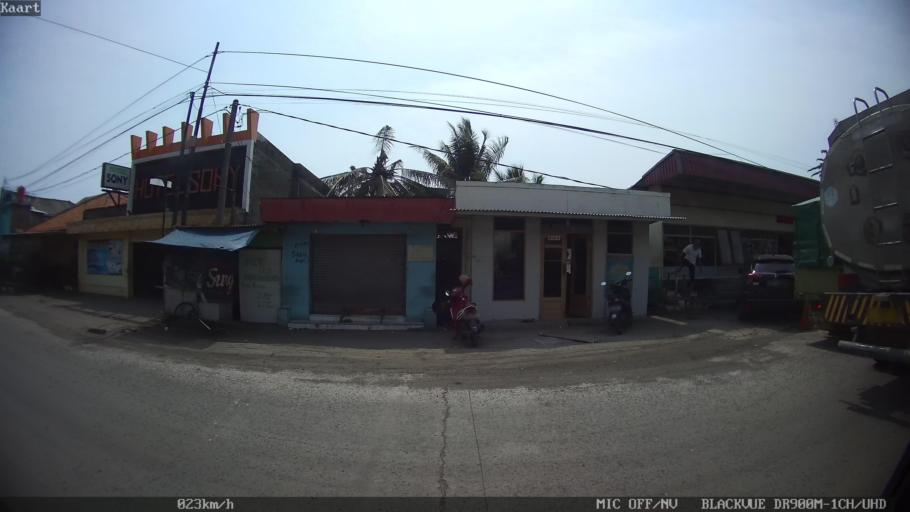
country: ID
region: Banten
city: Kubangkepuh
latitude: -5.9375
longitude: 106.0019
